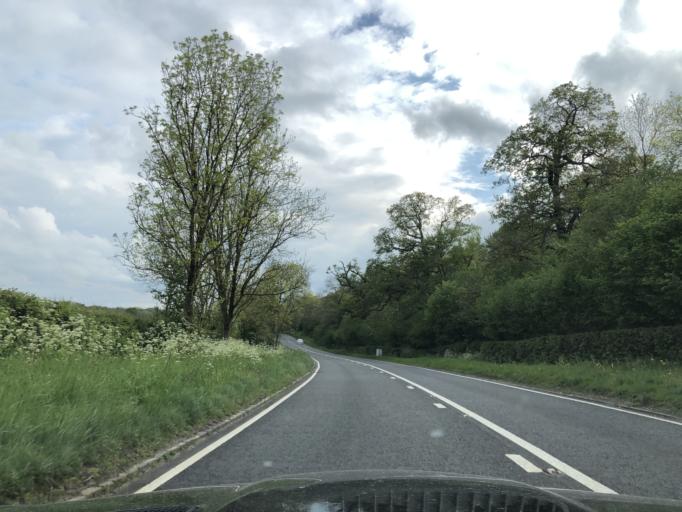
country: GB
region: England
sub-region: Gloucestershire
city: Moreton in Marsh
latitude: 52.0105
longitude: -1.6925
